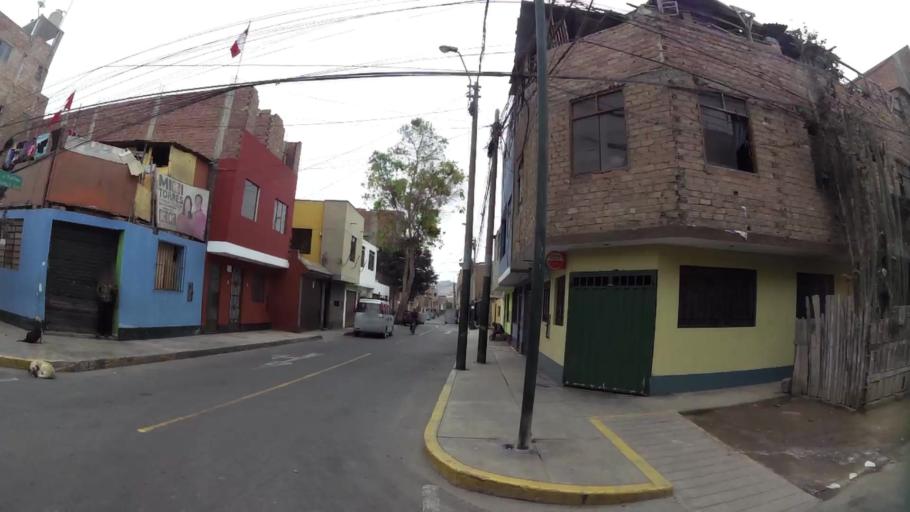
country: PE
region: Lima
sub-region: Lima
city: Surco
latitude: -12.1526
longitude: -77.0140
